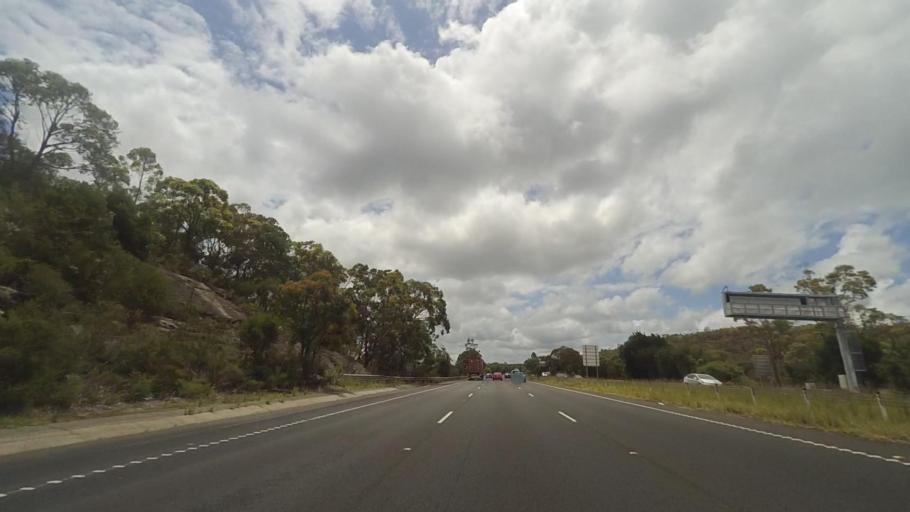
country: AU
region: New South Wales
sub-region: Gosford Shire
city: Point Clare
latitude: -33.4445
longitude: 151.2184
